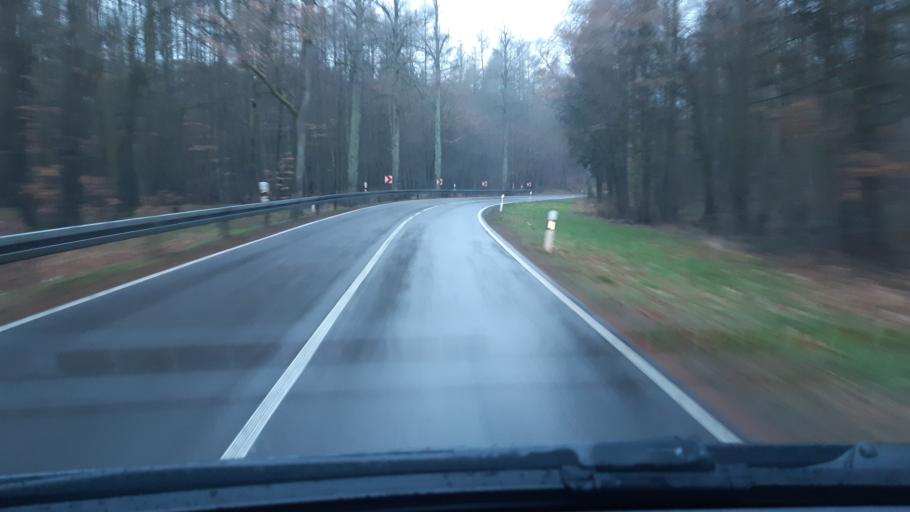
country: DE
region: Brandenburg
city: Mittenwalde
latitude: 53.1652
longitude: 13.6478
